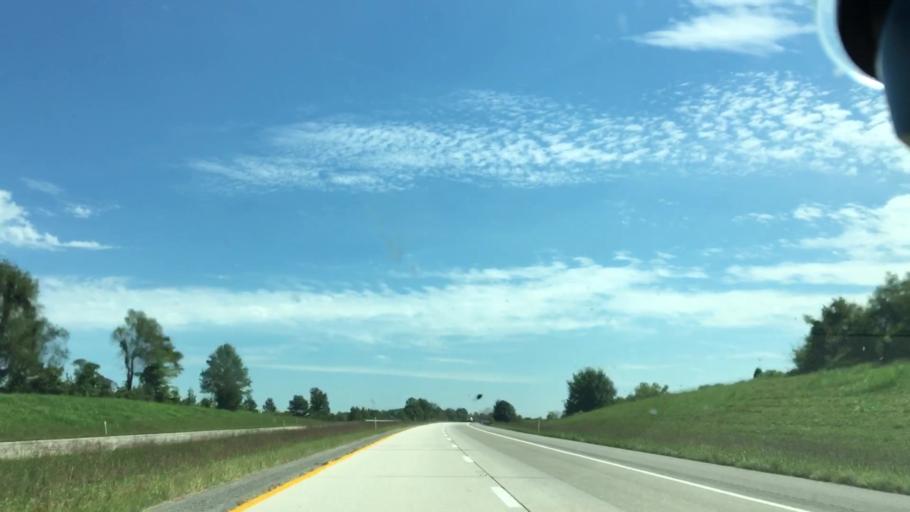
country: US
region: Kentucky
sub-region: Henderson County
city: Henderson
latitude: 37.7738
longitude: -87.4360
